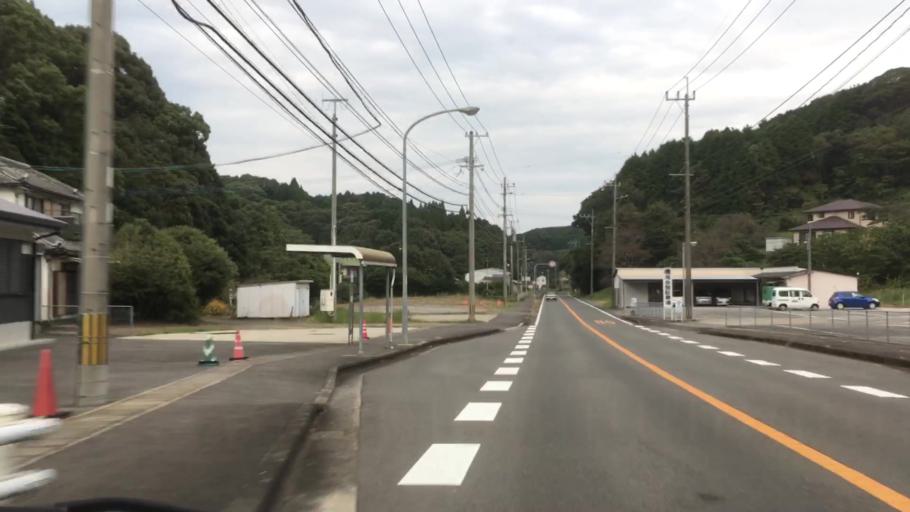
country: JP
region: Nagasaki
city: Togitsu
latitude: 32.9401
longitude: 129.6547
